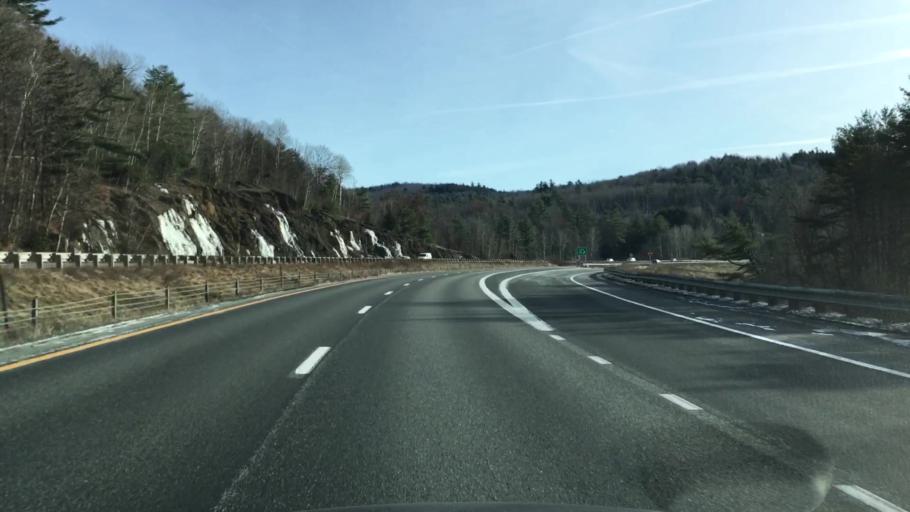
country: US
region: New Hampshire
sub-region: Grafton County
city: Enfield
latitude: 43.6004
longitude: -72.1676
